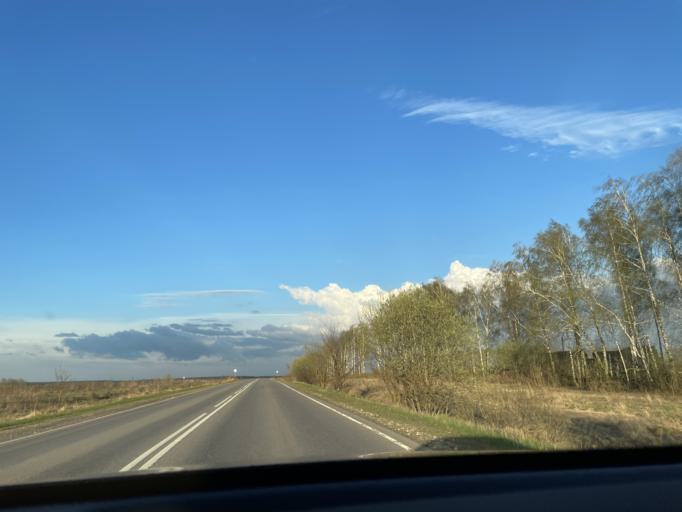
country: RU
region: Tula
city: Novogurovskiy
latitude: 54.5218
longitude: 37.4544
